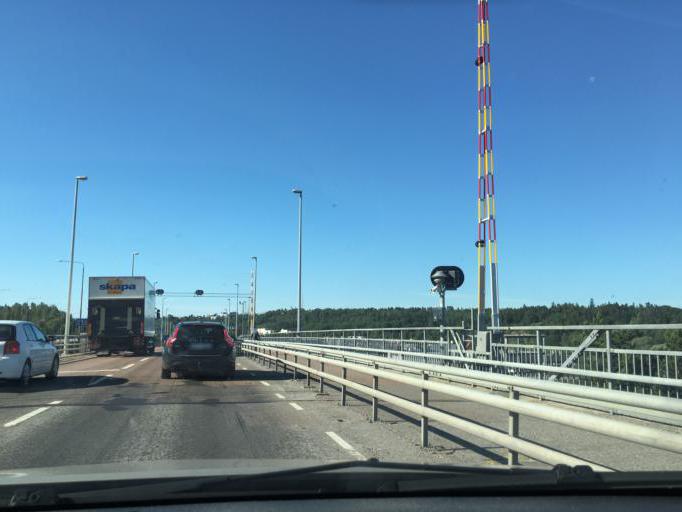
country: SE
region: Stockholm
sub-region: Sodertalje Kommun
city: Soedertaelje
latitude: 59.1848
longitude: 17.6423
